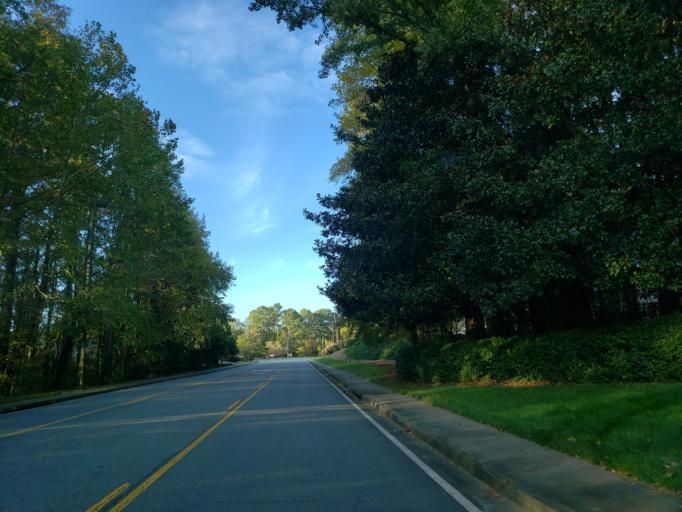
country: US
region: Georgia
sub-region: Cobb County
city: Kennesaw
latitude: 34.0061
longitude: -84.5905
